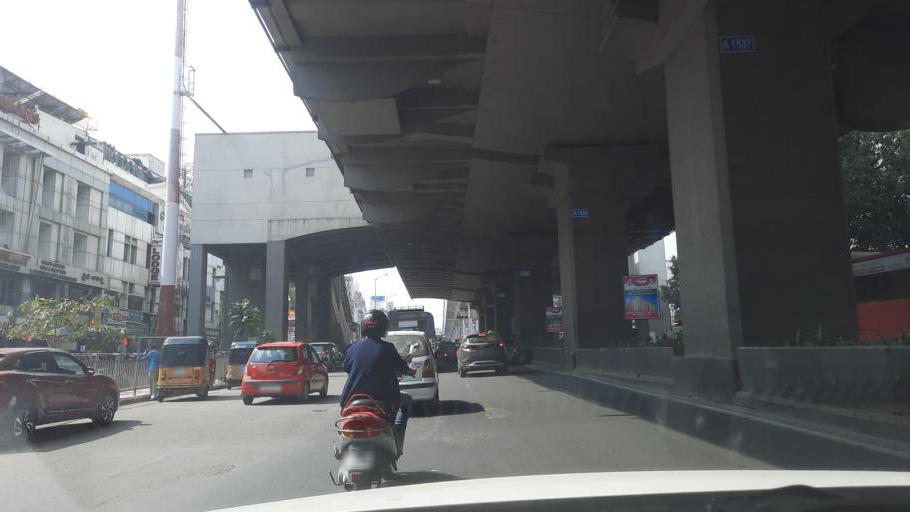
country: IN
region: Telangana
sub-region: Rangareddi
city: Gaddi Annaram
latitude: 17.3682
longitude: 78.5236
